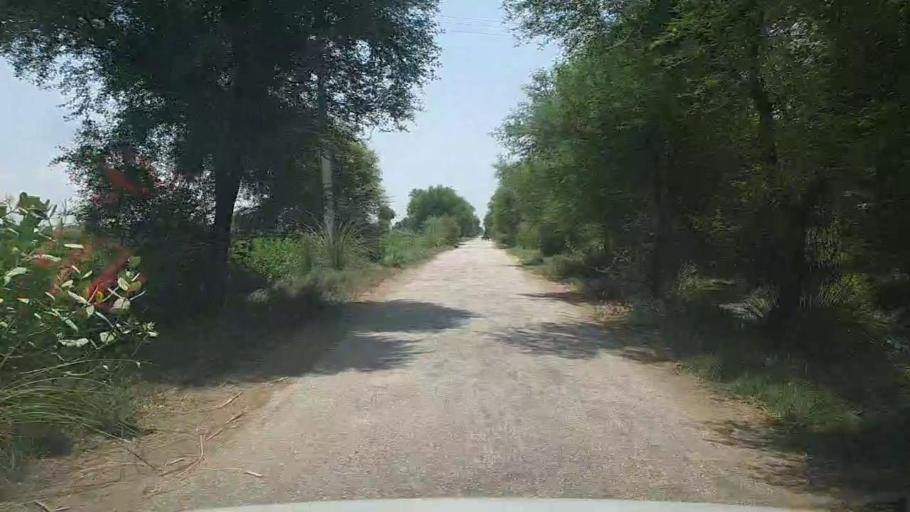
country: PK
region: Sindh
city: Ubauro
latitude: 28.1656
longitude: 69.7470
